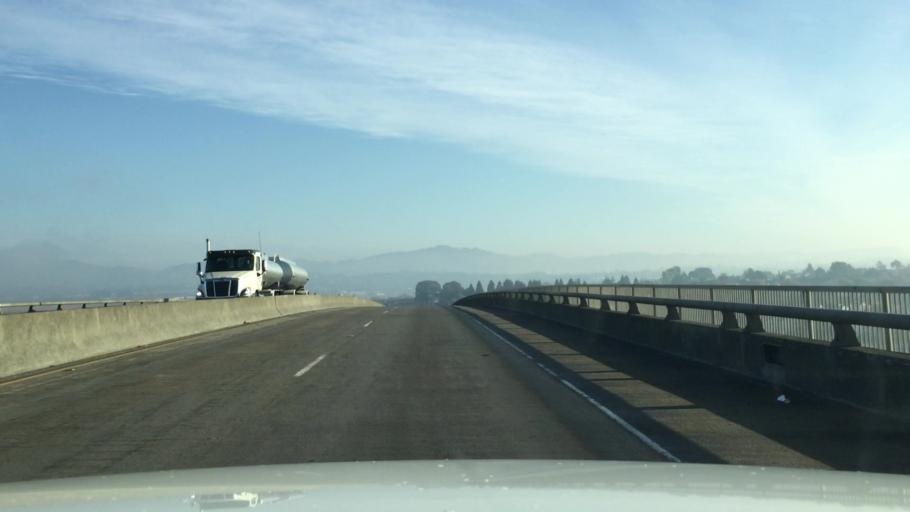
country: US
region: California
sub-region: Solano County
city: Vallejo
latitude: 38.1204
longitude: -122.2803
